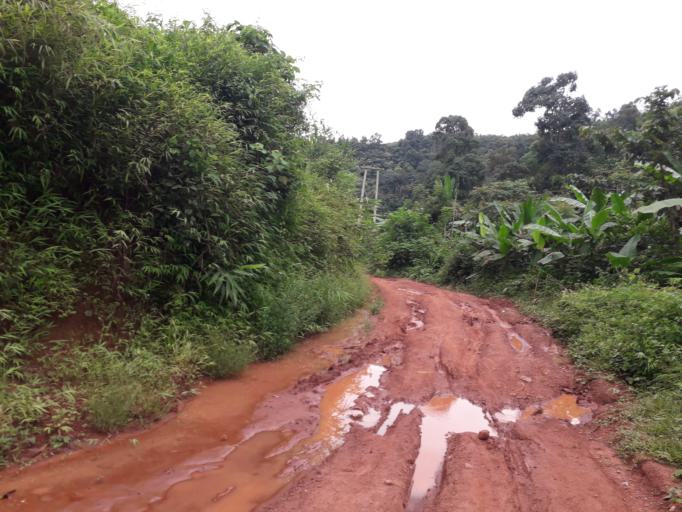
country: CN
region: Yunnan
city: Menglie
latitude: 22.1905
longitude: 101.7009
